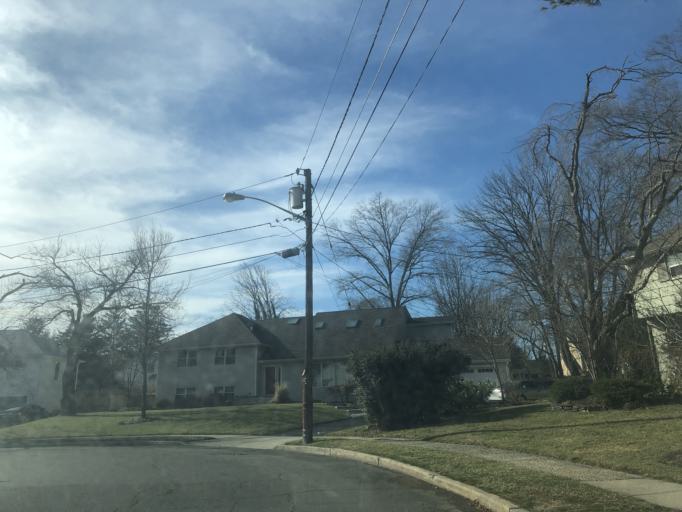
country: US
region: New Jersey
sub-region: Mercer County
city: Princeton
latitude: 40.3542
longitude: -74.6396
